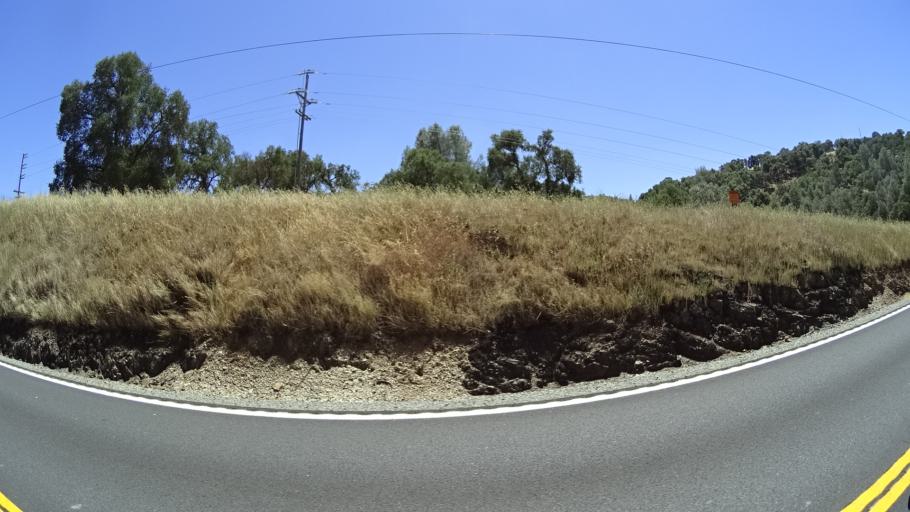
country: US
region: California
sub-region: Calaveras County
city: San Andreas
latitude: 38.2004
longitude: -120.7202
